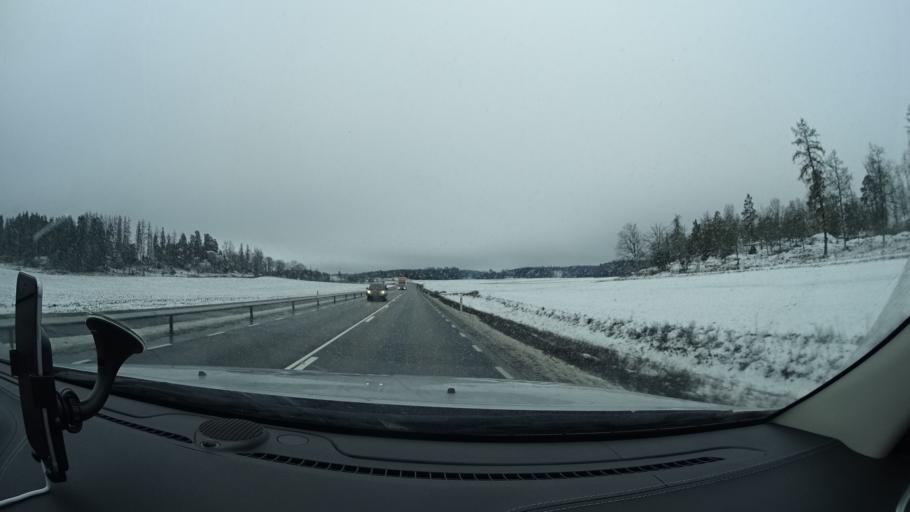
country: SE
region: OErebro
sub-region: Askersunds Kommun
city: Askersund
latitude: 58.8627
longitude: 14.9025
